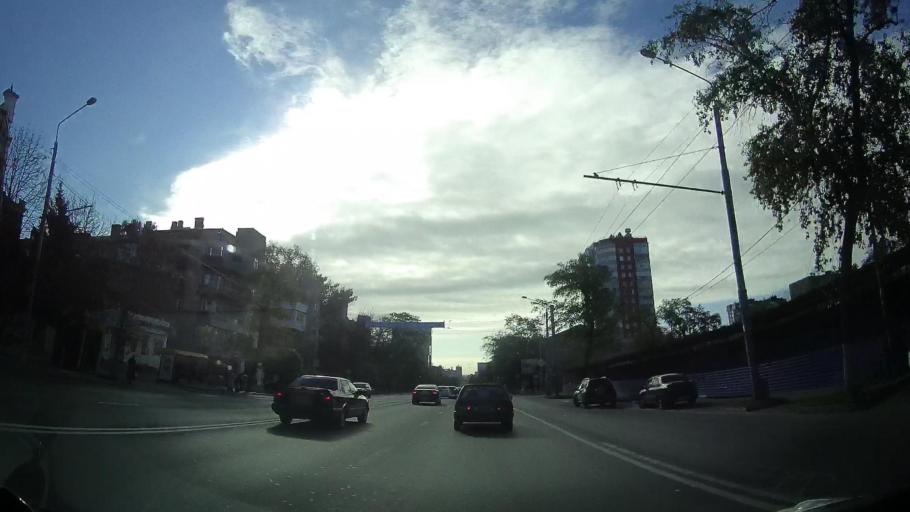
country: RU
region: Rostov
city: Rostov-na-Donu
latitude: 47.2300
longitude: 39.7031
